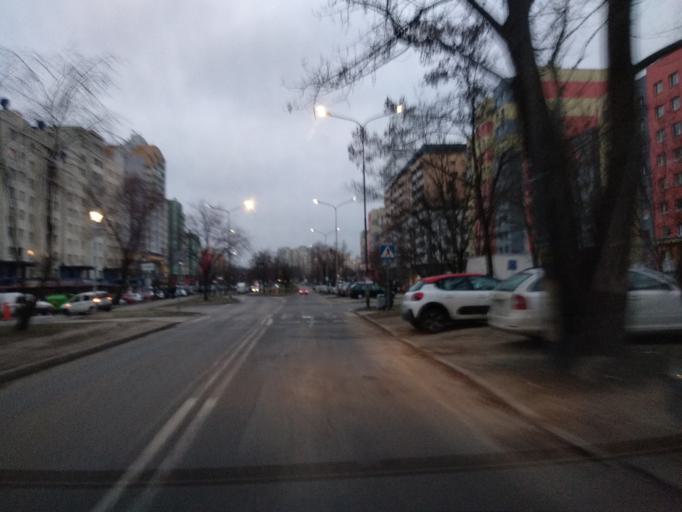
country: PL
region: Lower Silesian Voivodeship
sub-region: Powiat wroclawski
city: Wroclaw
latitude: 51.1278
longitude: 16.9698
